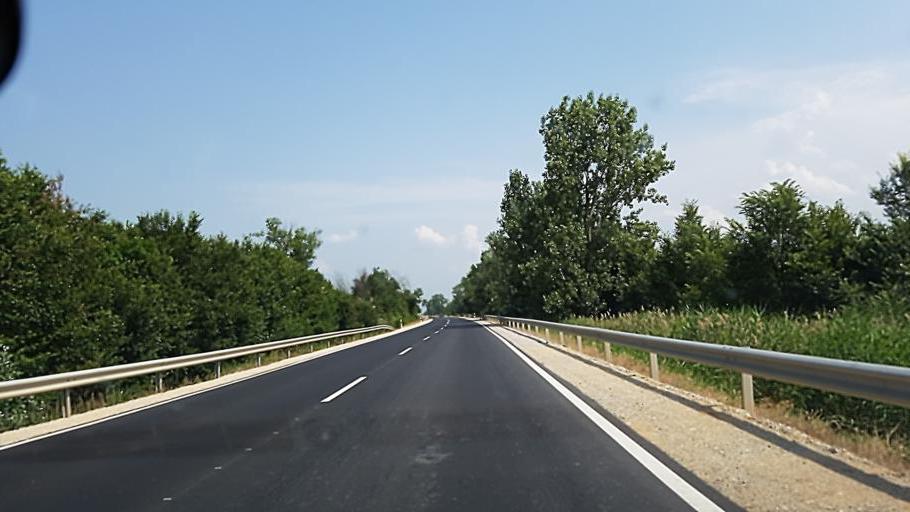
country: HU
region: Heves
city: Poroszlo
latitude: 47.6671
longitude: 20.5657
